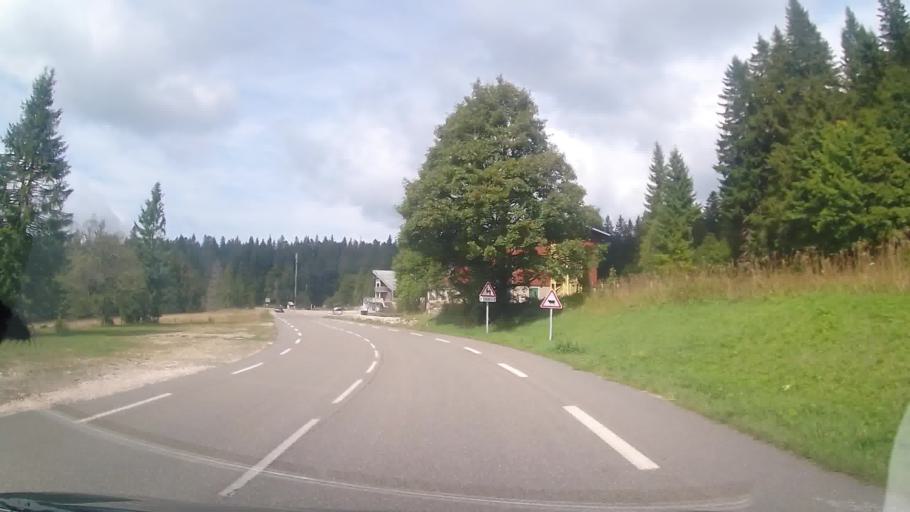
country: FR
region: Rhone-Alpes
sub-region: Departement de l'Ain
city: Gex
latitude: 46.3875
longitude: 6.0533
